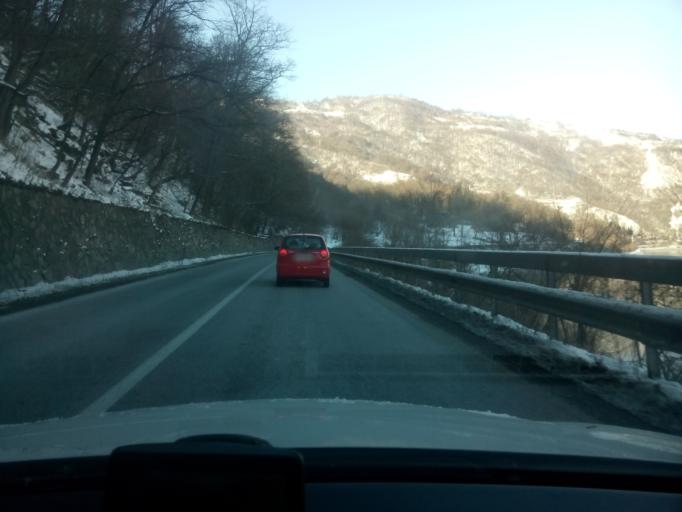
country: RO
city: Cainenii Mici
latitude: 45.4760
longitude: 24.2920
